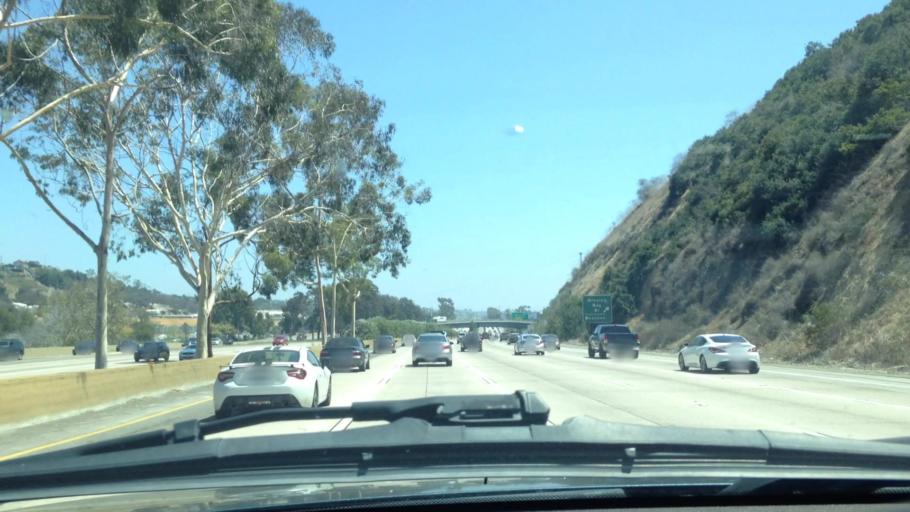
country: US
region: California
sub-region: San Diego County
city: La Jolla
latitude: 32.8157
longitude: -117.2231
